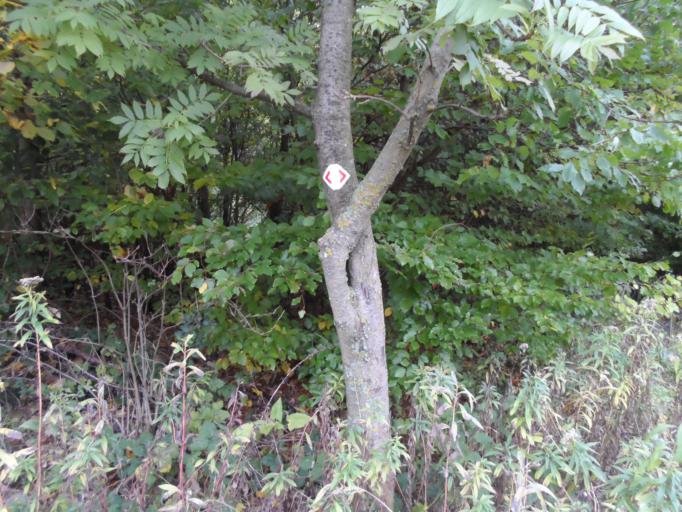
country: HU
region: Veszprem
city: Zirc
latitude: 47.3334
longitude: 17.8974
